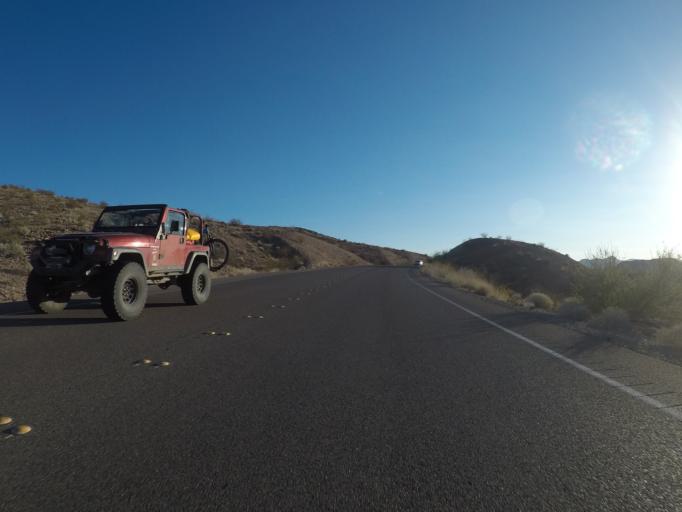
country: US
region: Nevada
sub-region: Clark County
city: Moapa Valley
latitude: 36.2976
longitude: -114.4908
